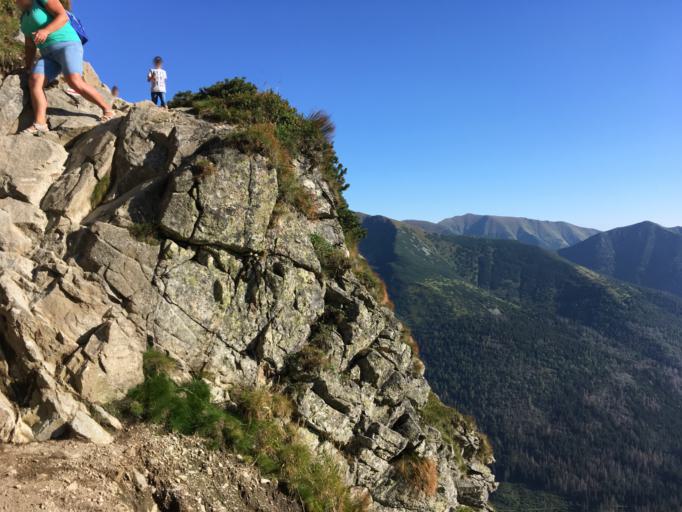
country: PL
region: Lesser Poland Voivodeship
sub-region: Powiat tatrzanski
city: Zakopane
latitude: 49.2329
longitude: 19.9479
